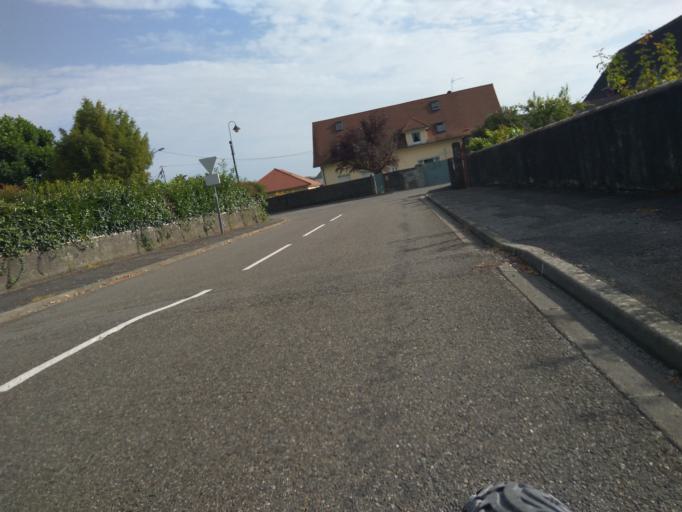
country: FR
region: Aquitaine
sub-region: Departement des Pyrenees-Atlantiques
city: Mazeres-Lezons
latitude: 43.2703
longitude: -0.3425
